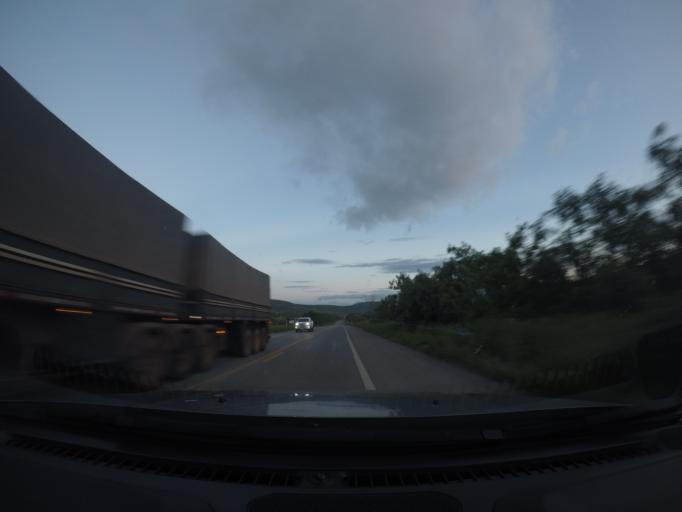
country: BR
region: Bahia
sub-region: Seabra
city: Seabra
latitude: -12.4268
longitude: -41.7619
